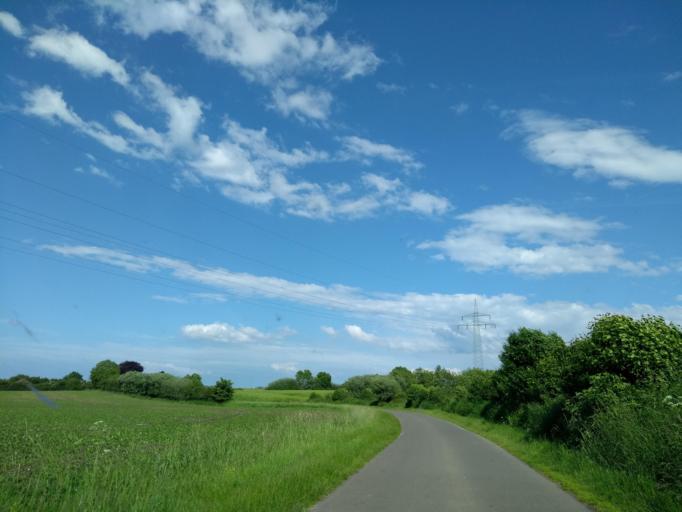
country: DE
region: Schleswig-Holstein
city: Damp
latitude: 54.5604
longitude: 9.9666
